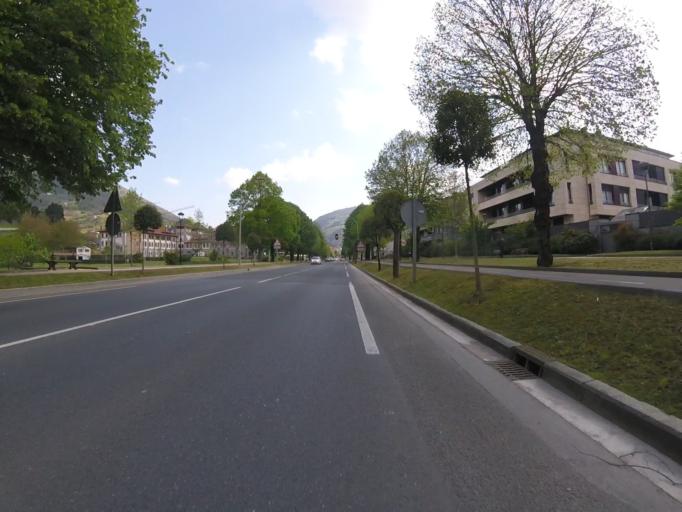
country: ES
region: Basque Country
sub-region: Provincia de Guipuzcoa
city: Azpeitia
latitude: 43.1786
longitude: -2.2746
